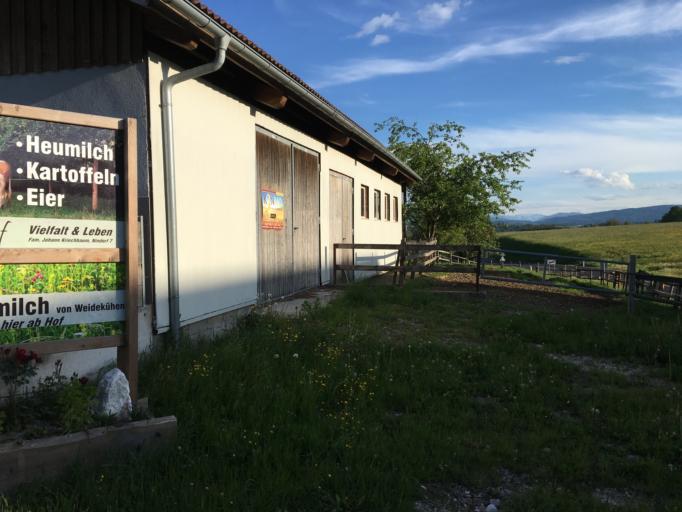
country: AT
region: Upper Austria
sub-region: Politischer Bezirk Vocklabruck
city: Pfaffing
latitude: 48.0186
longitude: 13.4870
